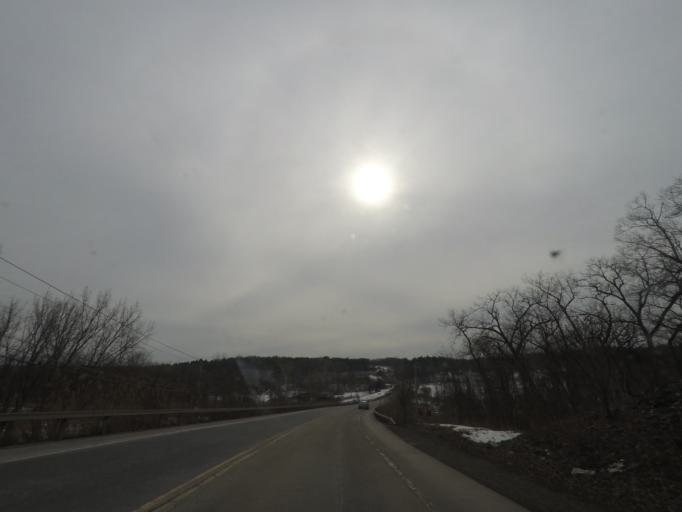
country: US
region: New York
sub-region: Albany County
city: Voorheesville
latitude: 42.6801
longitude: -73.9051
